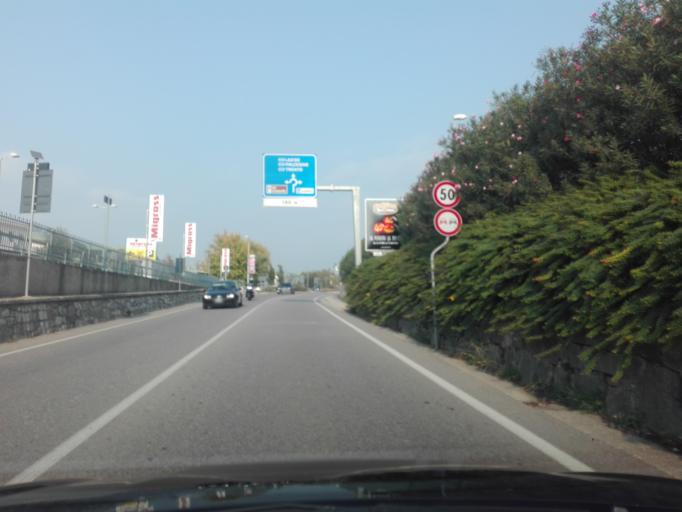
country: IT
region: Veneto
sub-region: Provincia di Verona
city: Cavalcaselle
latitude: 45.4446
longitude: 10.7067
